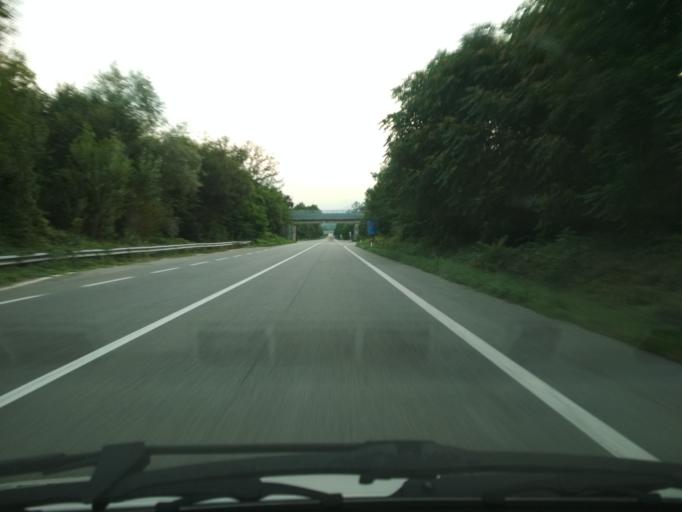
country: IT
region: Piedmont
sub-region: Provincia di Torino
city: Torre Canavese
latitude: 45.3987
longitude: 7.7523
